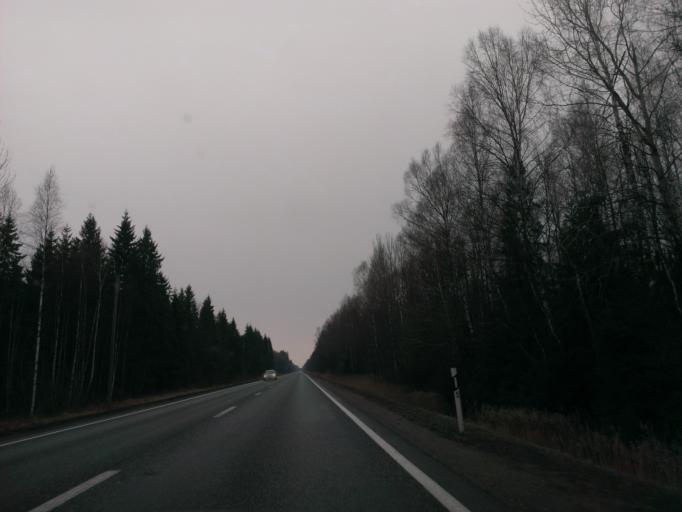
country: LV
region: Salacgrivas
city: Salacgriva
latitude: 57.5990
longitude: 24.4105
